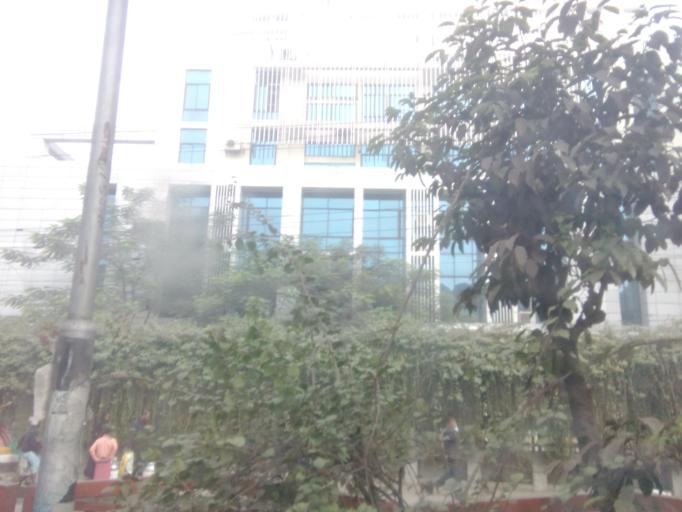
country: BD
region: Dhaka
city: Azimpur
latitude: 23.7384
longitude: 90.3941
